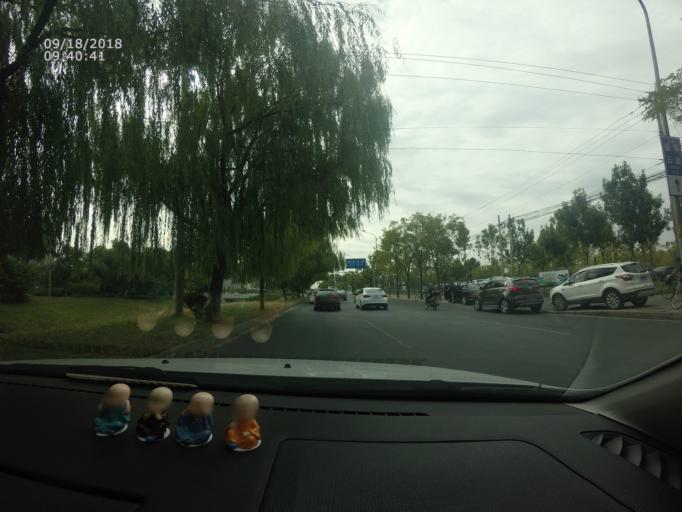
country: CN
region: Beijing
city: Xibeiwang
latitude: 40.0676
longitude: 116.2399
